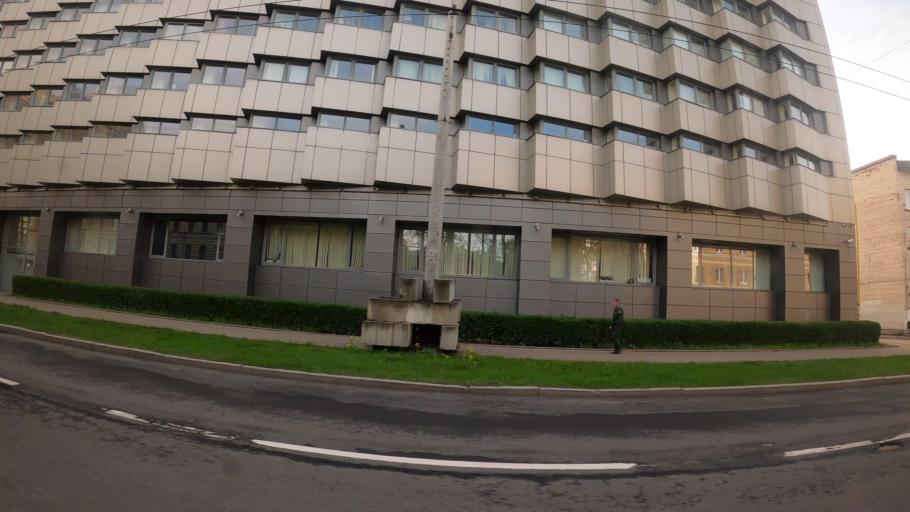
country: RU
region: St.-Petersburg
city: Vasyl'evsky Ostrov
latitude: 59.9332
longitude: 30.2483
